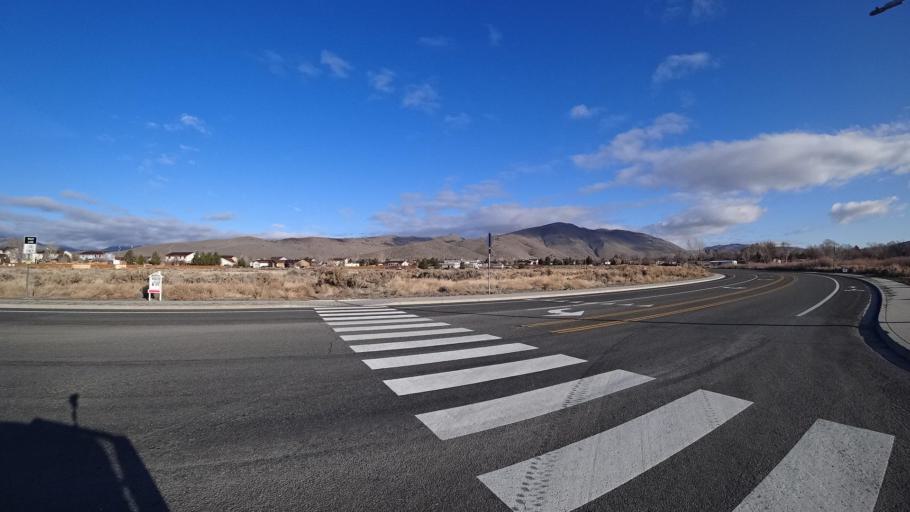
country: US
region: Nevada
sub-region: Washoe County
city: Cold Springs
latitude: 39.6758
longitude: -119.9792
